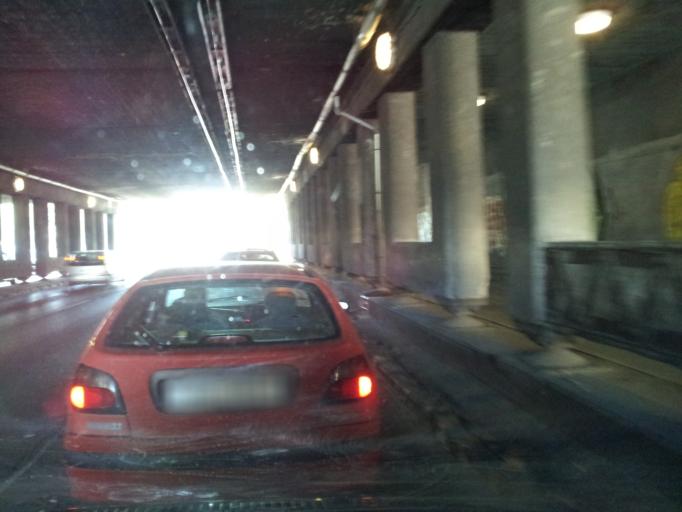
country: HU
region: Budapest
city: Budapest XIII. keruelet
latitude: 47.5183
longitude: 19.0729
